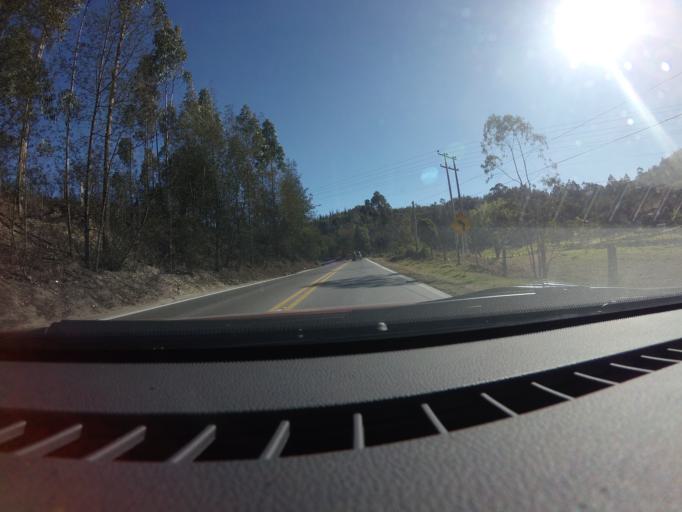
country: CO
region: Cundinamarca
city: Sutatausa
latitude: 5.2604
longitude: -73.8474
